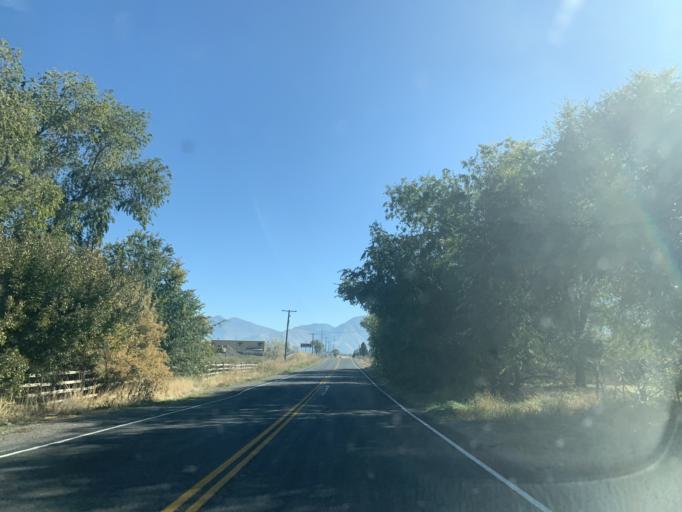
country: US
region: Utah
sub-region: Utah County
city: West Mountain
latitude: 40.0411
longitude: -111.7703
